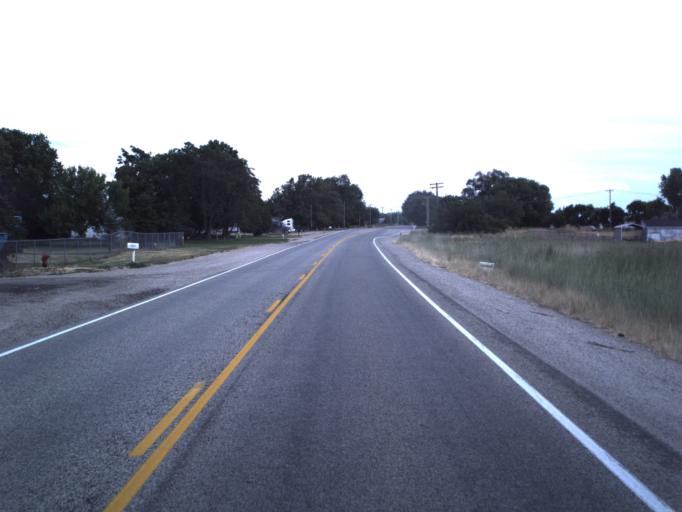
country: US
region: Utah
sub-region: Weber County
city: Farr West
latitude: 41.3148
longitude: -112.0280
